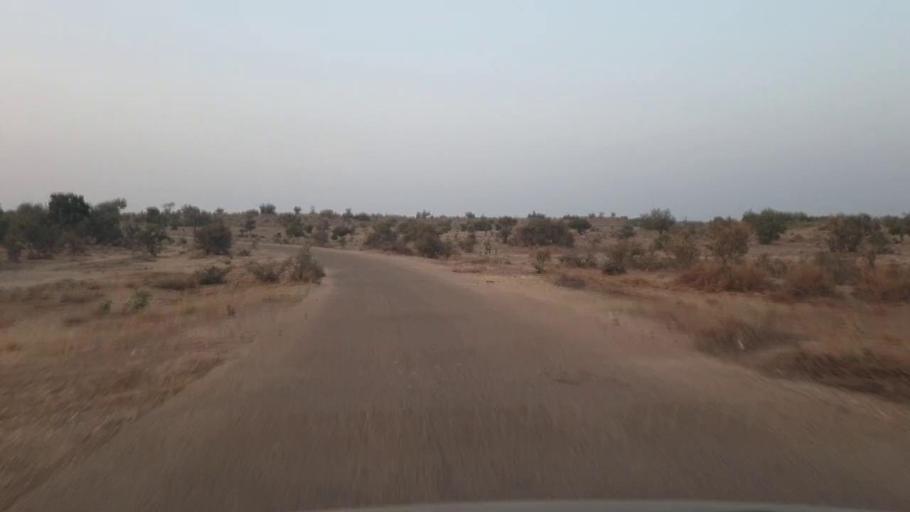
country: PK
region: Sindh
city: Umarkot
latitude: 25.3350
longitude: 70.0578
